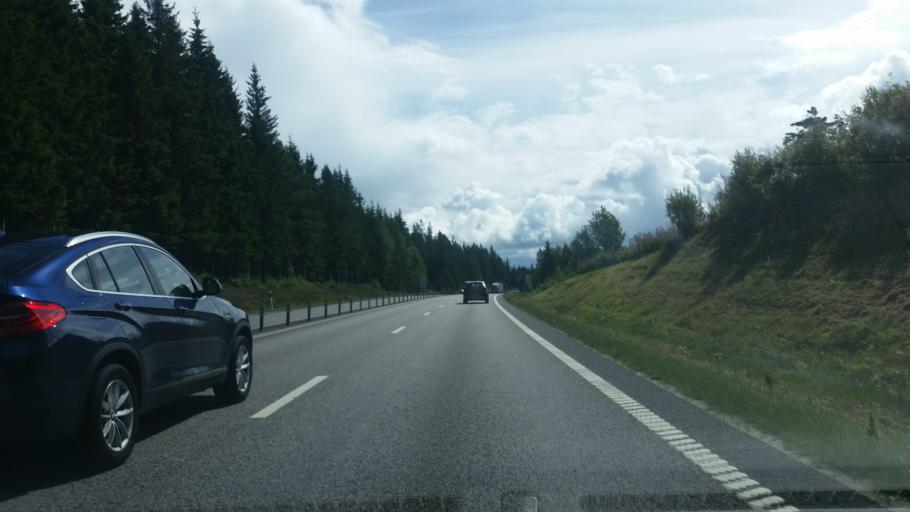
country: SE
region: Joenkoeping
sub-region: Mullsjo Kommun
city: Mullsjoe
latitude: 57.7719
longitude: 13.7111
